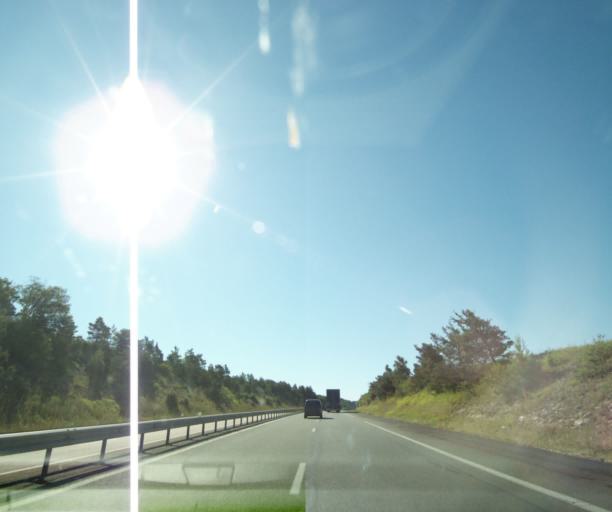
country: FR
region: Champagne-Ardenne
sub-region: Departement de l'Aube
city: Ville-sous-la-Ferte
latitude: 48.0986
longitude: 4.8159
